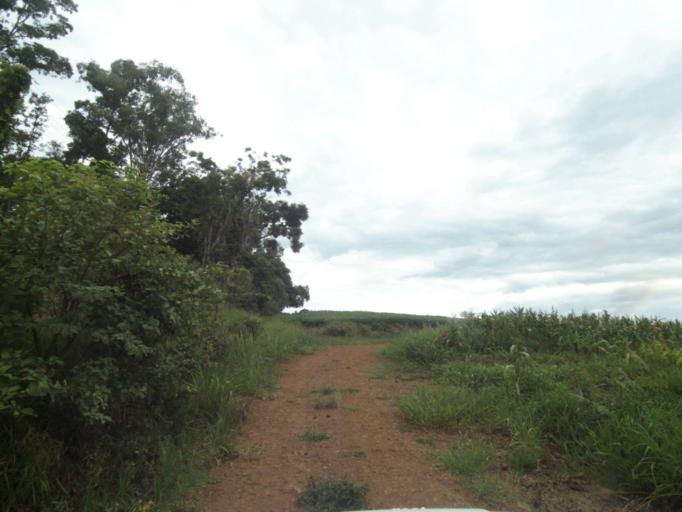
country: BR
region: Parana
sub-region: Guaraniacu
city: Guaraniacu
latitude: -24.9213
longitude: -52.9357
